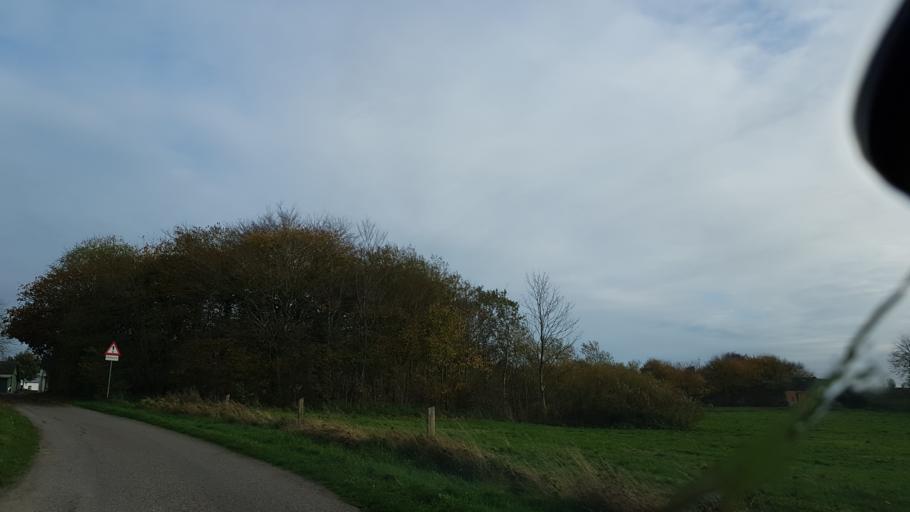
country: DK
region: South Denmark
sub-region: Haderslev Kommune
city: Gram
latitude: 55.2601
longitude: 9.1163
